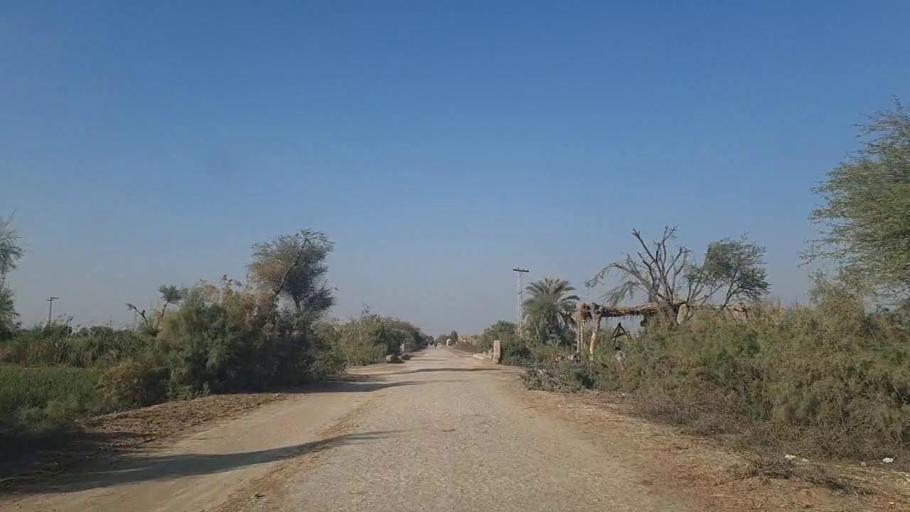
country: PK
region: Sindh
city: Jam Sahib
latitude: 26.3182
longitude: 68.7148
